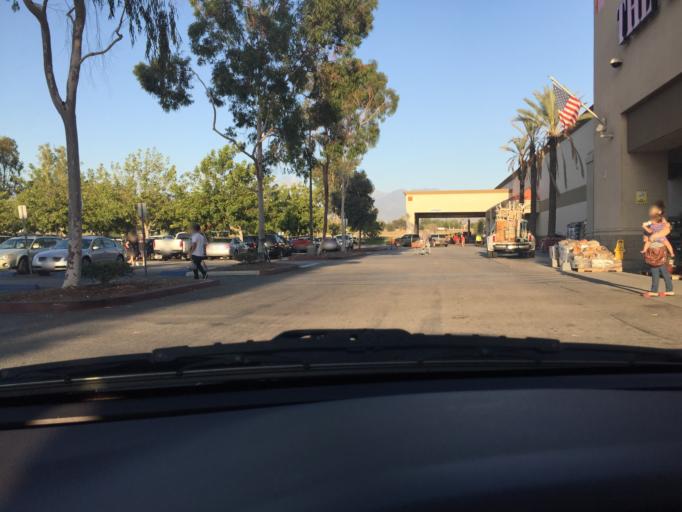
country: US
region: California
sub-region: San Bernardino County
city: Redlands
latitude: 34.0688
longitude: -117.1982
